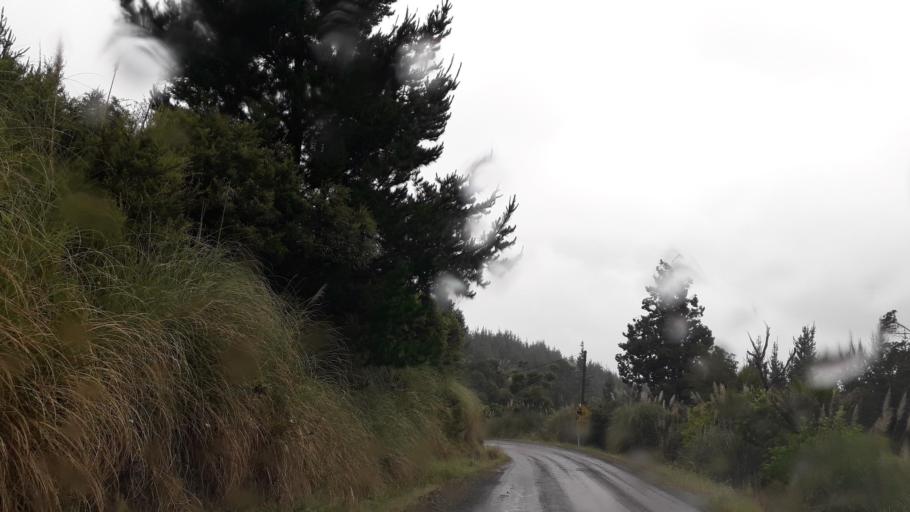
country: NZ
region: Northland
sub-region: Far North District
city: Kaitaia
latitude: -35.3681
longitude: 173.4114
